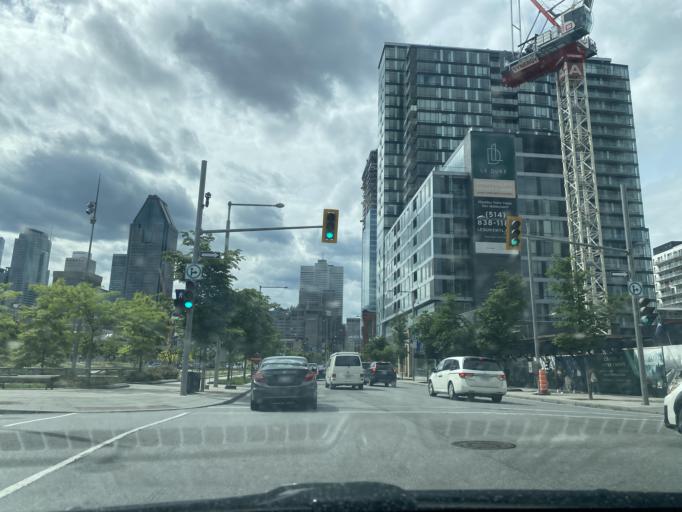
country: CA
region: Quebec
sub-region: Montreal
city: Montreal
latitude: 45.4968
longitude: -73.5572
